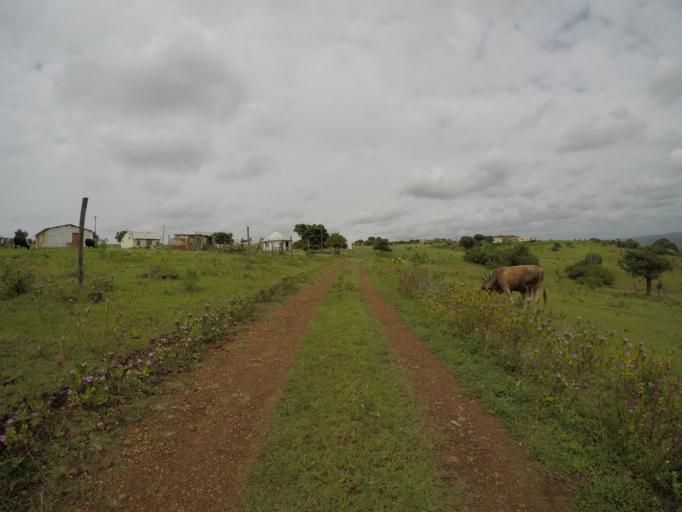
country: ZA
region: KwaZulu-Natal
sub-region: uThungulu District Municipality
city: Empangeni
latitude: -28.6153
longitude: 31.8982
